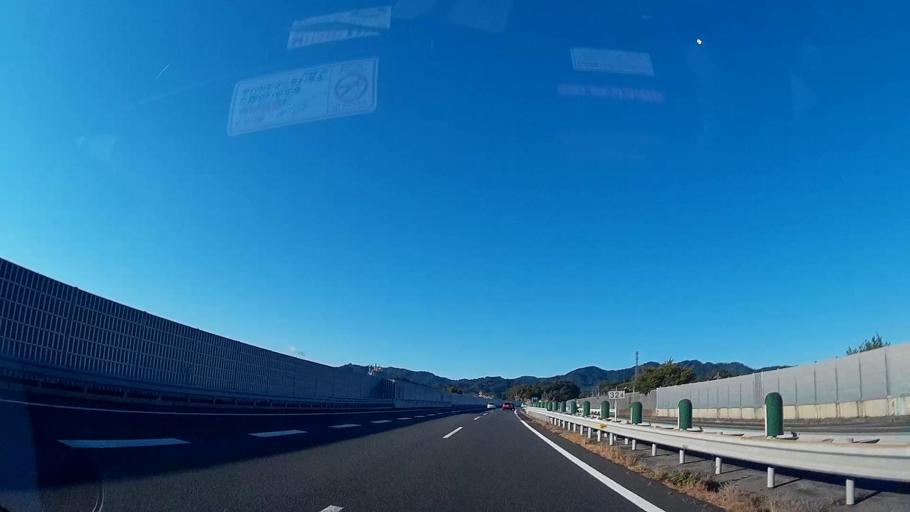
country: JP
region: Tokyo
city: Hachioji
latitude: 35.6598
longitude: 139.2830
